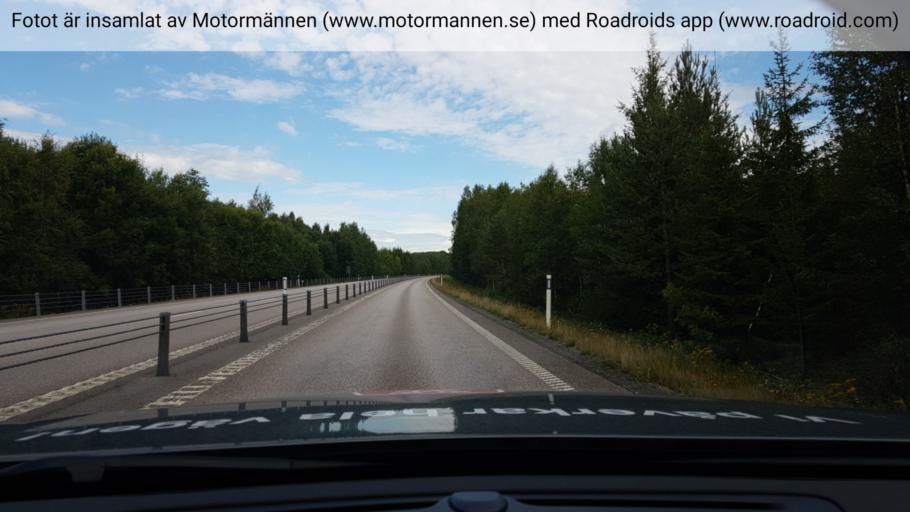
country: SE
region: Uppsala
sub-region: Heby Kommun
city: Tarnsjo
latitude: 60.2755
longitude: 16.9323
